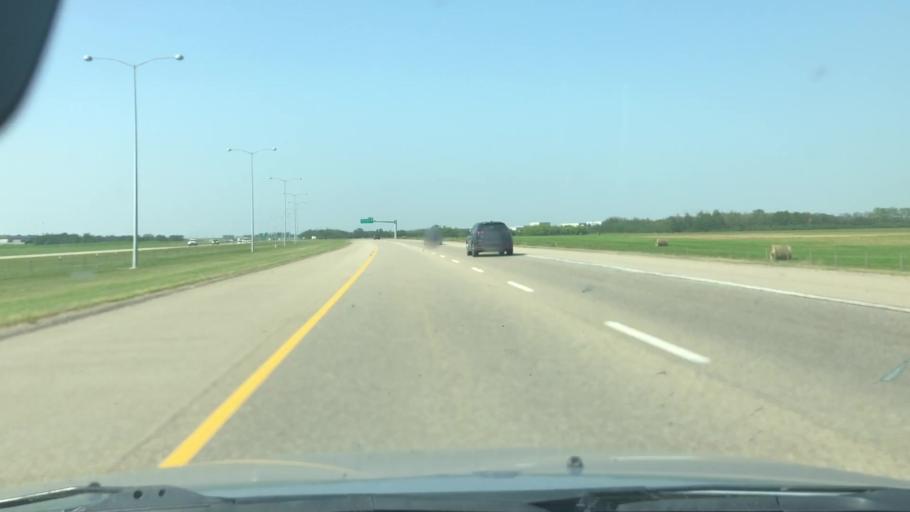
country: CA
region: Alberta
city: Edmonton
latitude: 53.6463
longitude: -113.5194
